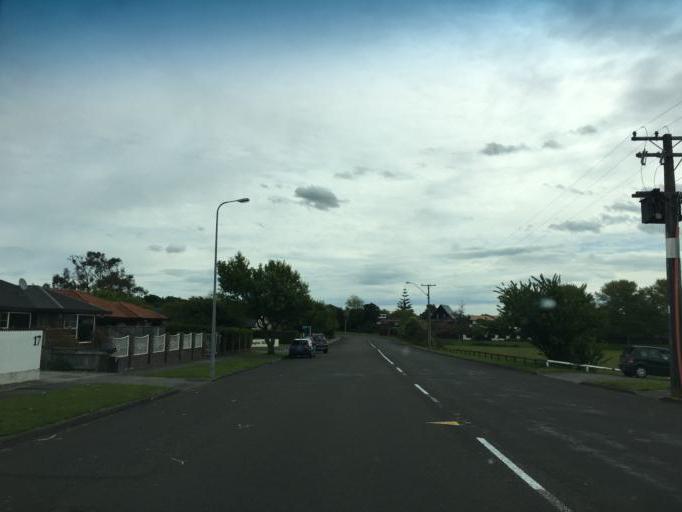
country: NZ
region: Manawatu-Wanganui
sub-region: Palmerston North City
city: Palmerston North
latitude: -40.3764
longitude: 175.5809
